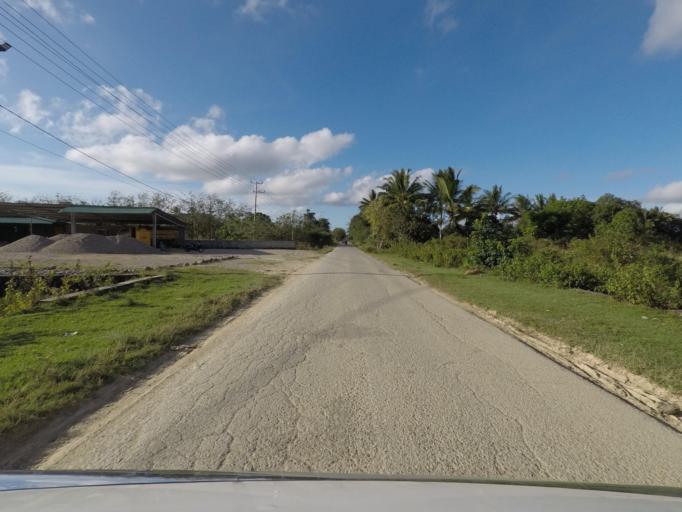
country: TL
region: Lautem
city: Lospalos
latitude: -8.4647
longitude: 126.9958
